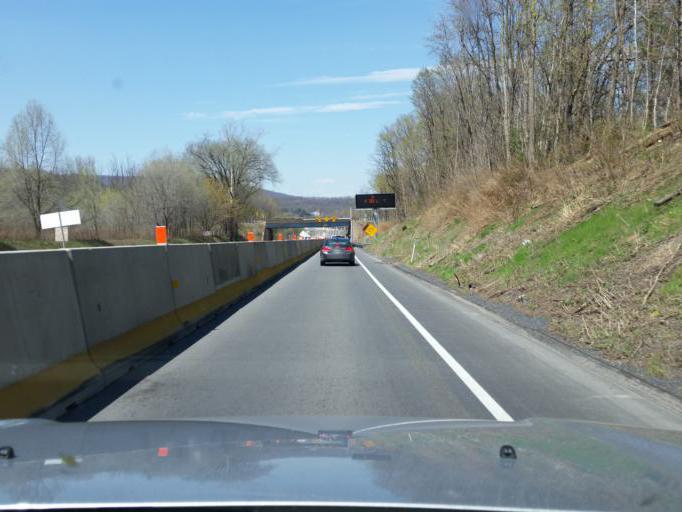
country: US
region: Pennsylvania
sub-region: Mifflin County
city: Lewistown
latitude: 40.5974
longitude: -77.5599
